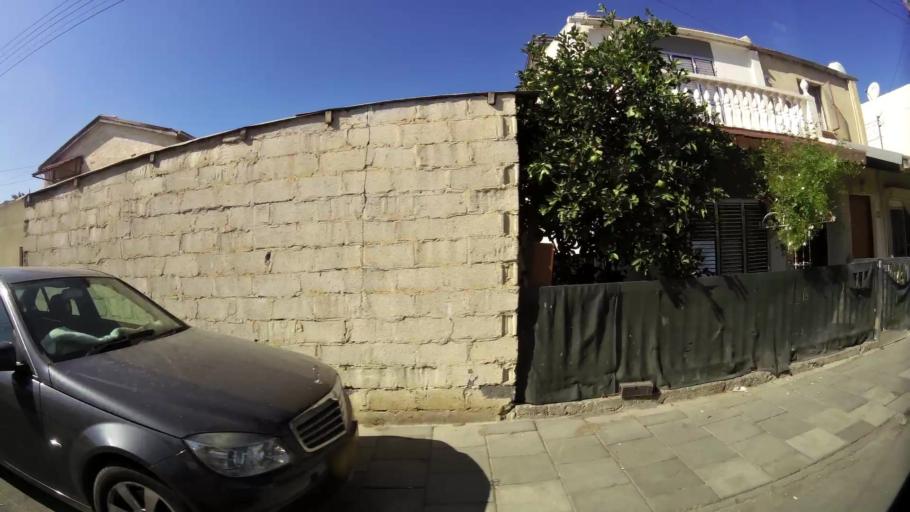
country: CY
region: Lefkosia
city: Nicosia
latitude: 35.2073
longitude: 33.3354
